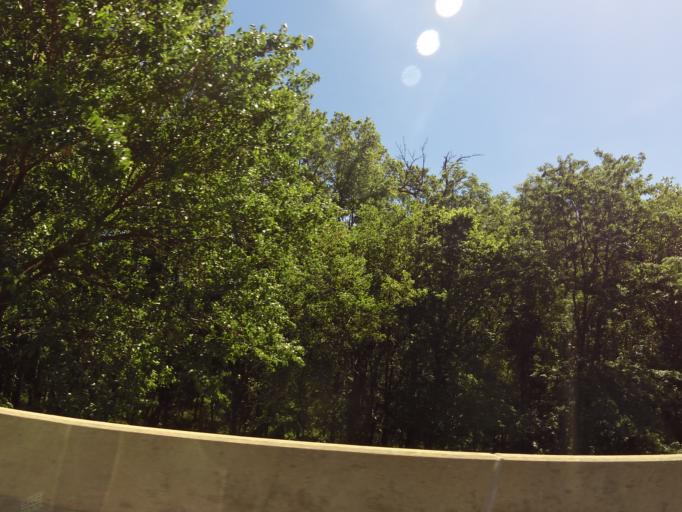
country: US
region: Illinois
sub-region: Vermilion County
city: Rossville
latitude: 40.3310
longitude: -87.6611
